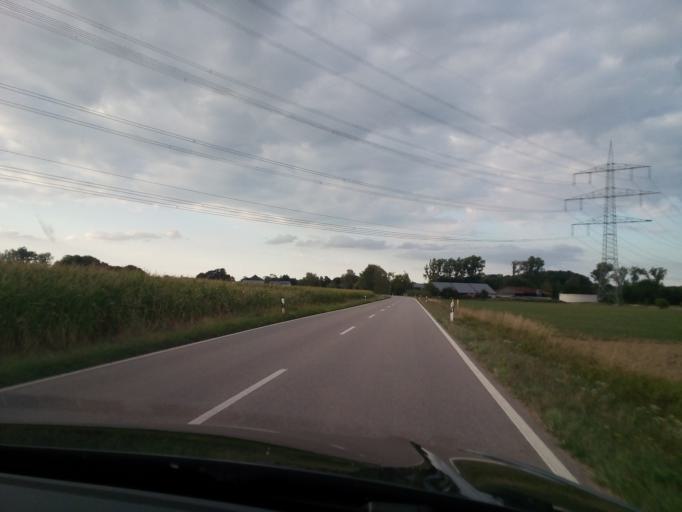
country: DE
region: Baden-Wuerttemberg
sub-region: Freiburg Region
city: Rheinau
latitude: 48.6660
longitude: 7.9942
